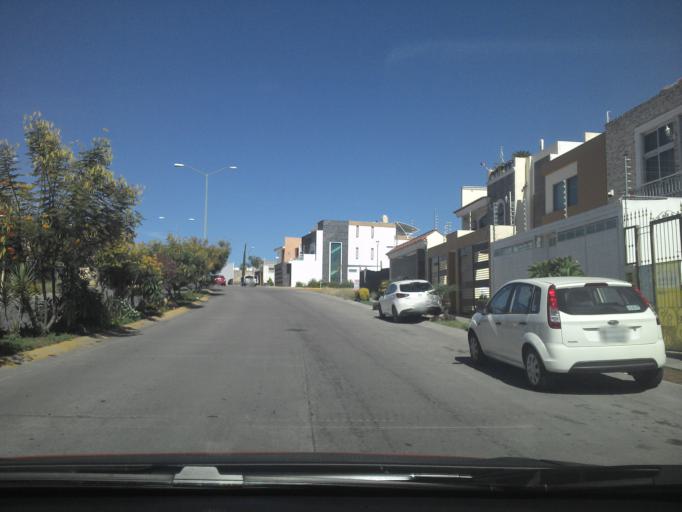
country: MX
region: Jalisco
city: Zapopan2
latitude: 20.7468
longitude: -103.4116
